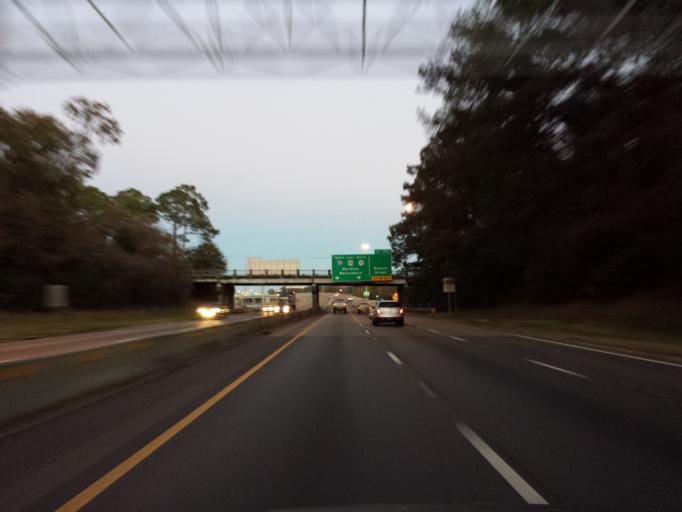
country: US
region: Mississippi
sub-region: Jones County
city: Laurel
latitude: 31.6842
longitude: -89.1438
